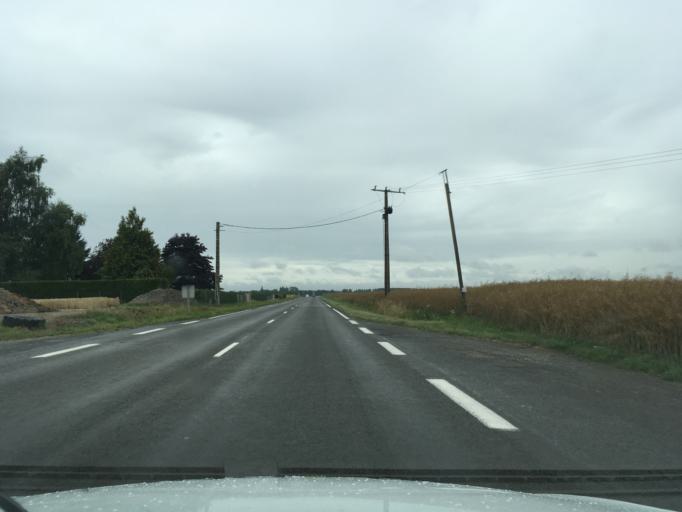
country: FR
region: Picardie
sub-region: Departement de l'Aisne
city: Esqueheries
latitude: 49.9290
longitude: 3.7021
